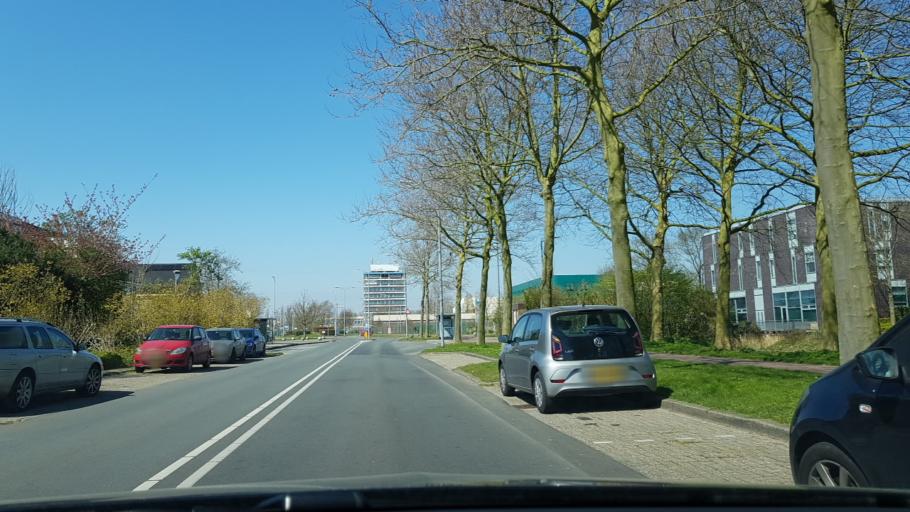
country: NL
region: South Holland
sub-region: Gemeente Hillegom
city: Hillegom
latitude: 52.2712
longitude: 4.6333
